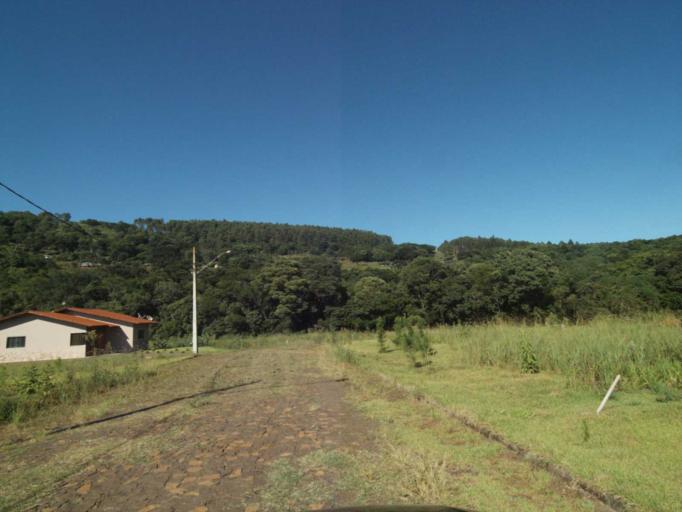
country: BR
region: Parana
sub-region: Francisco Beltrao
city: Francisco Beltrao
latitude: -26.1431
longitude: -53.3171
